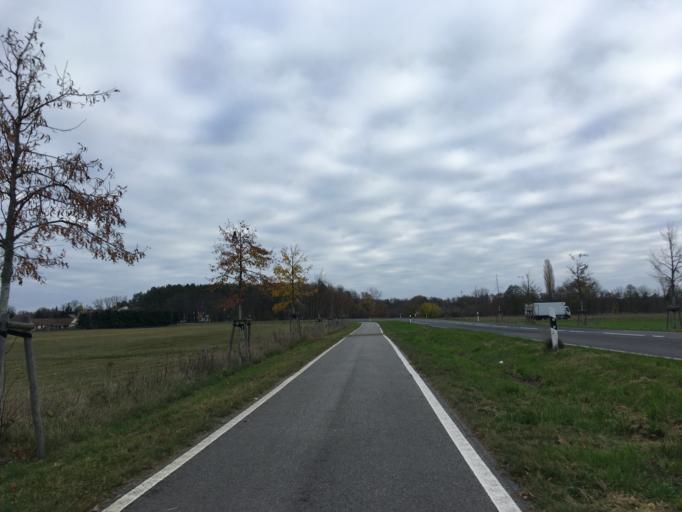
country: DE
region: Brandenburg
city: Burg
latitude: 51.8102
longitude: 14.1203
